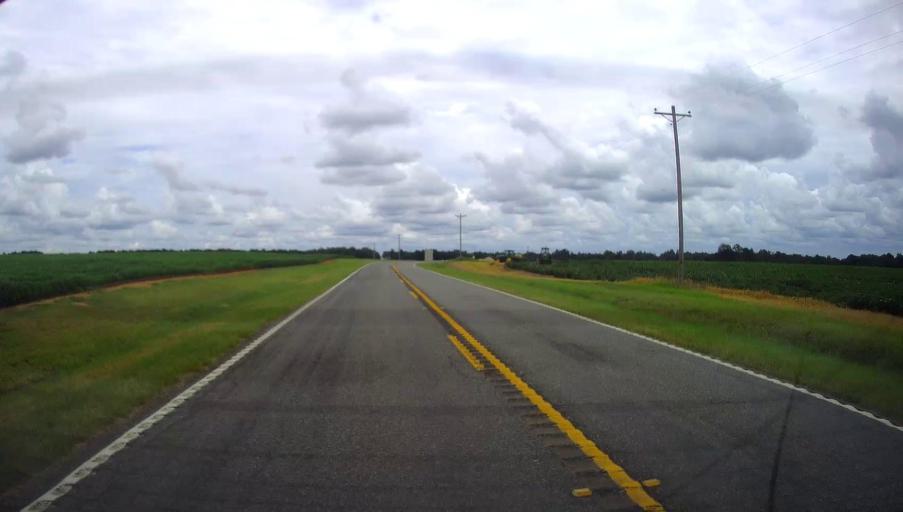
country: US
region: Georgia
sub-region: Dooly County
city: Unadilla
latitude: 32.2908
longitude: -83.8322
